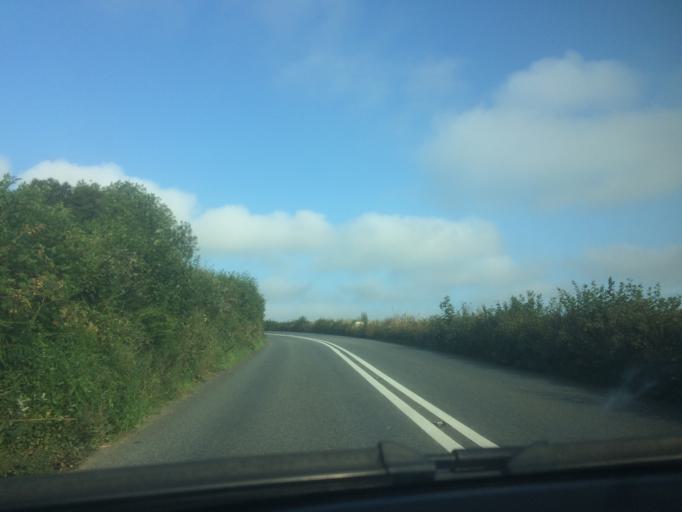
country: GB
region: England
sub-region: Cornwall
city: Gunnislake
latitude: 50.5356
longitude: -4.1795
